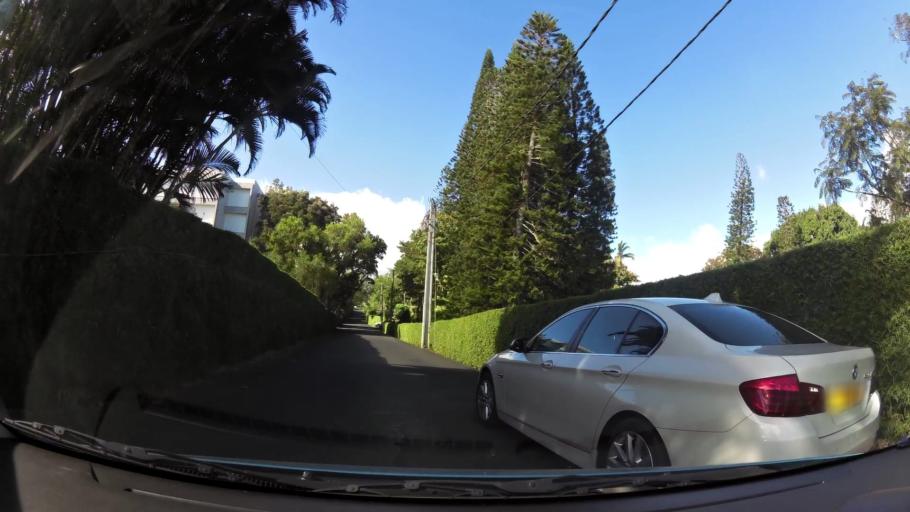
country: MU
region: Plaines Wilhems
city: Curepipe
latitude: -20.3098
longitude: 57.5024
